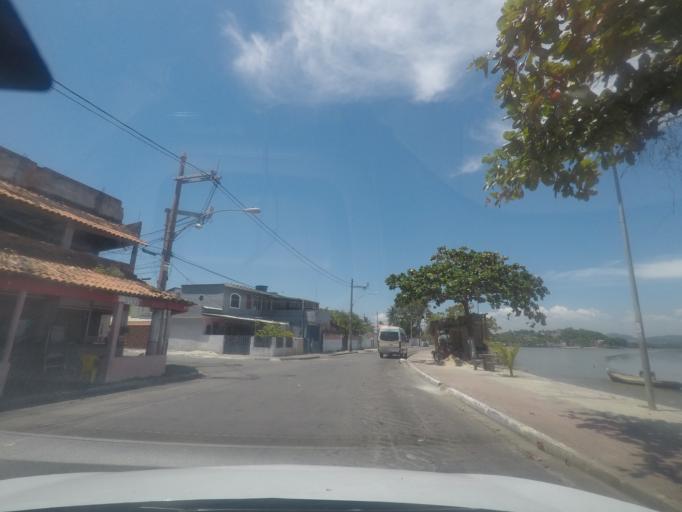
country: BR
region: Rio de Janeiro
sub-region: Itaguai
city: Itaguai
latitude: -22.9883
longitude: -43.6891
